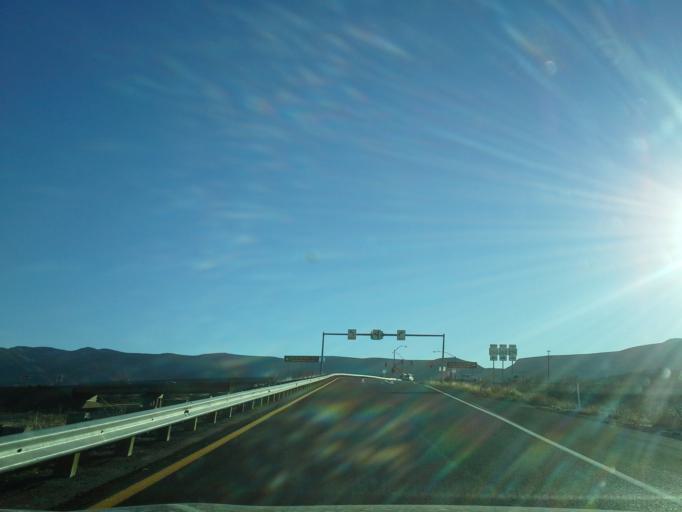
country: US
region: Arizona
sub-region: Yavapai County
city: Camp Verde
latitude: 34.5806
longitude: -111.8833
